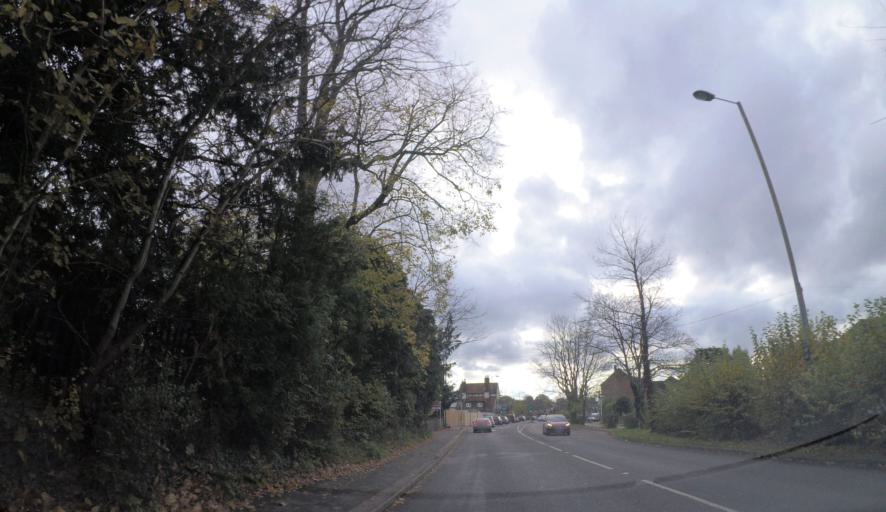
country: GB
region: England
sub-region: Surrey
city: Reigate
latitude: 51.2253
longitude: -0.1998
